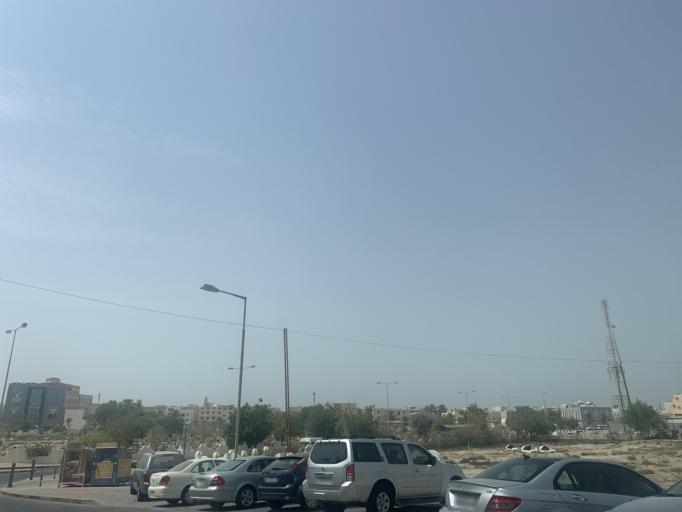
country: BH
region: Manama
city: Jidd Hafs
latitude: 26.2125
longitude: 50.4617
